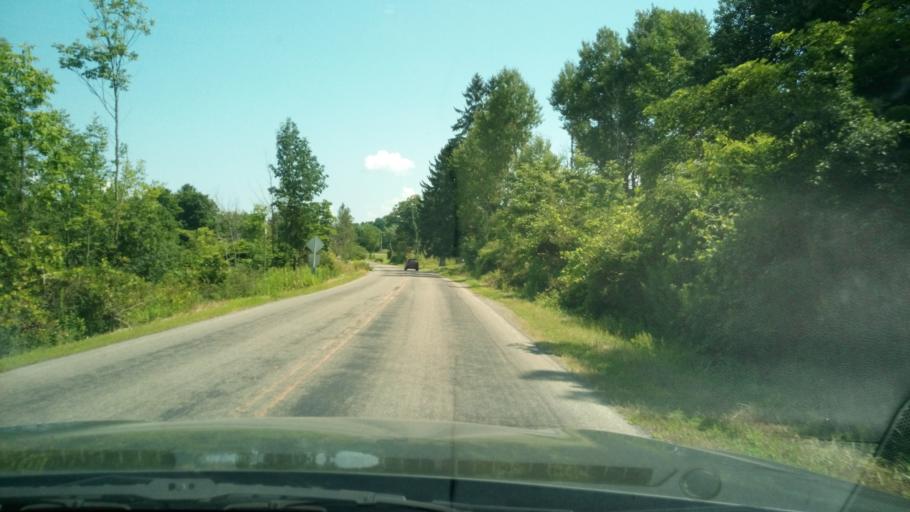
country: US
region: New York
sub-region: Chemung County
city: Horseheads North
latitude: 42.2730
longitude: -76.7973
